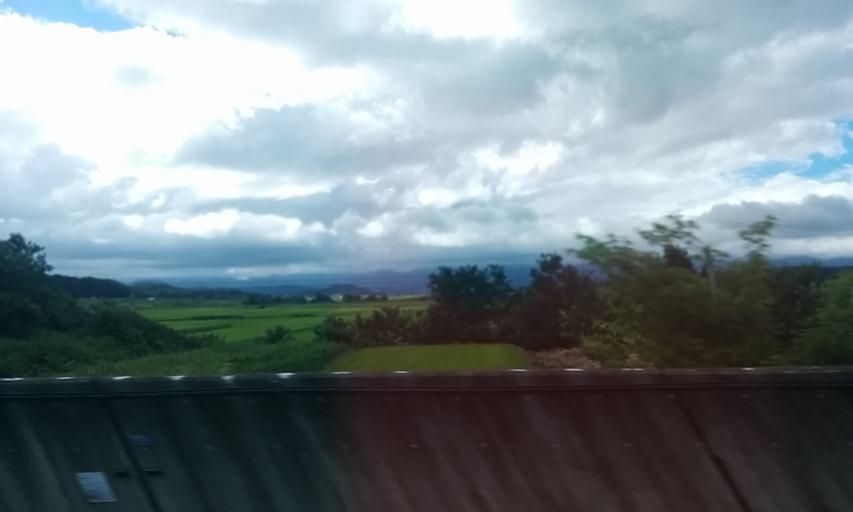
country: JP
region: Fukushima
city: Sukagawa
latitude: 37.2575
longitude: 140.3076
